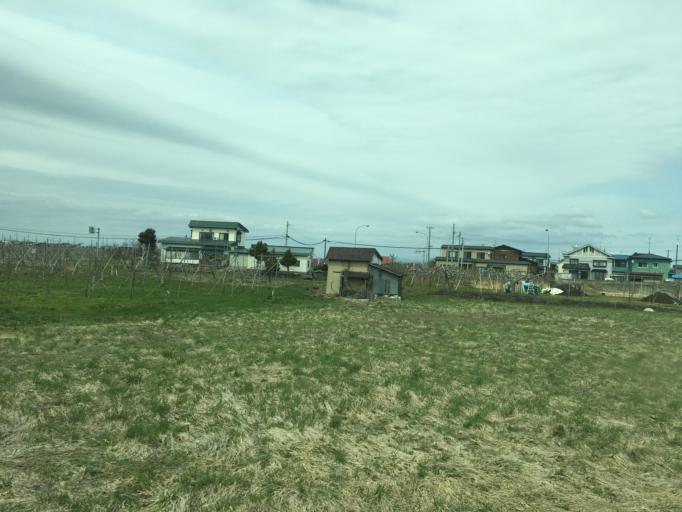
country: JP
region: Aomori
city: Hirosaki
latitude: 40.6439
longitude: 140.5159
